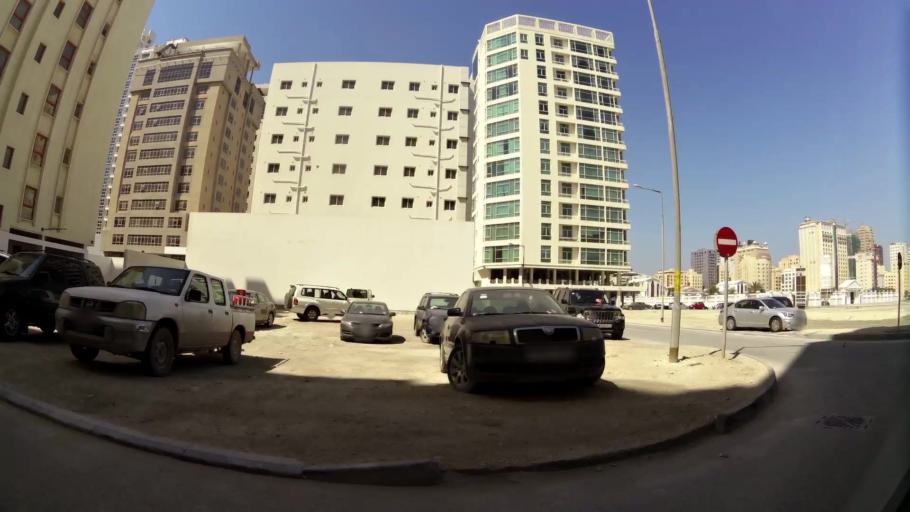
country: BH
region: Manama
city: Manama
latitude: 26.2144
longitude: 50.6076
